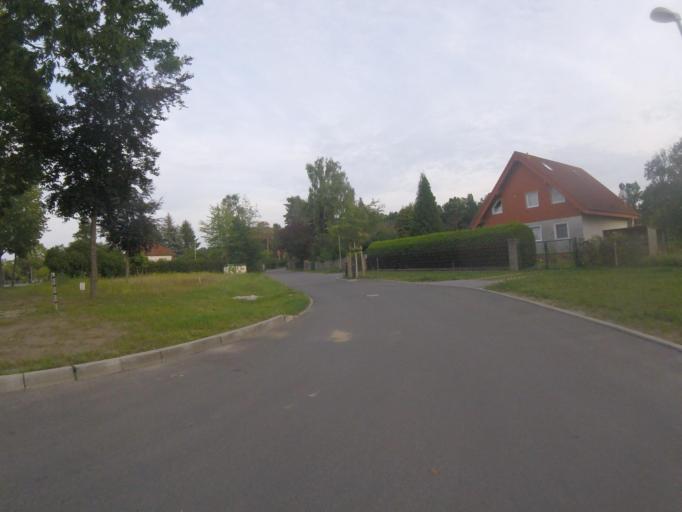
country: DE
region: Brandenburg
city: Wildau
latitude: 52.3340
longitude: 13.6189
